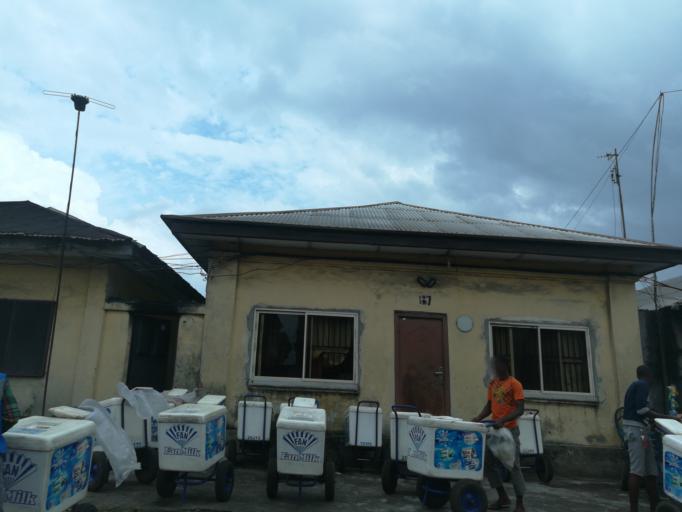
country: NG
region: Rivers
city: Port Harcourt
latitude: 4.7604
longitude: 7.0314
